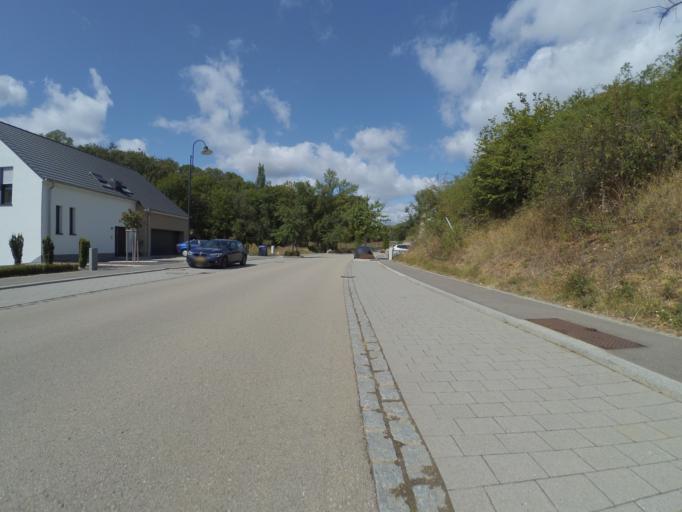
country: LU
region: Grevenmacher
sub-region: Canton de Remich
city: Lenningen
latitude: 49.6231
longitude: 6.3482
